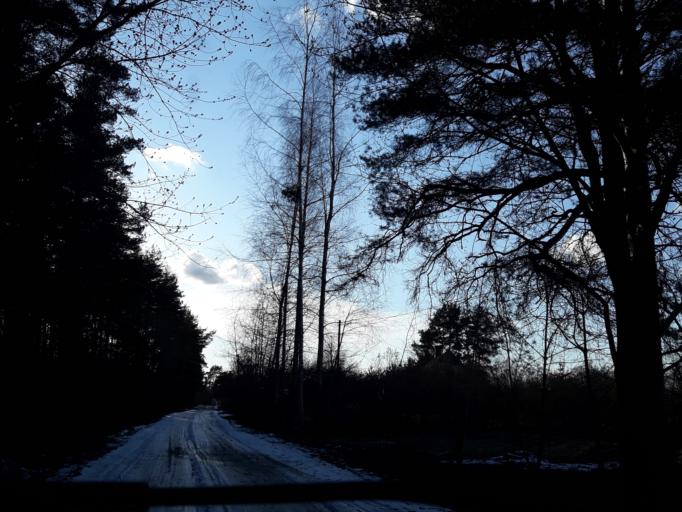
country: LV
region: Kekava
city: Kekava
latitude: 56.8739
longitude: 24.2109
